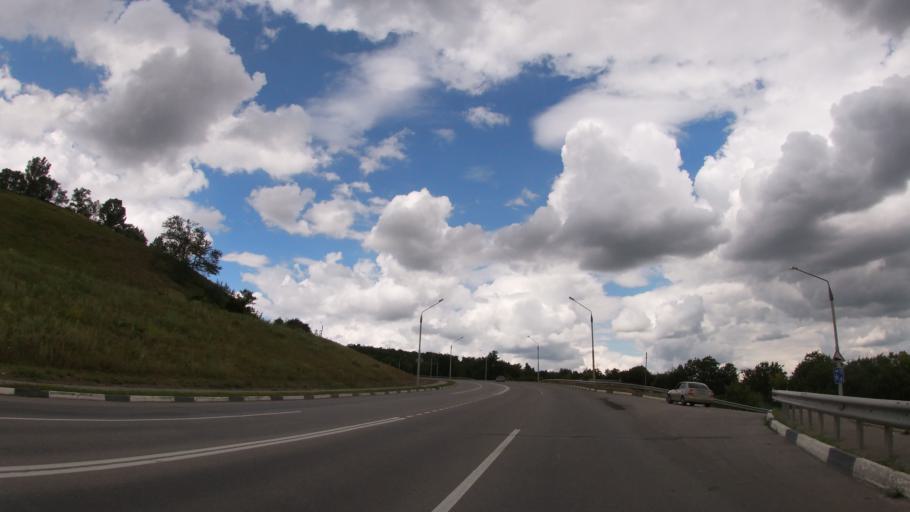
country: RU
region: Belgorod
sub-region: Belgorodskiy Rayon
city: Belgorod
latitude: 50.6189
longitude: 36.6164
